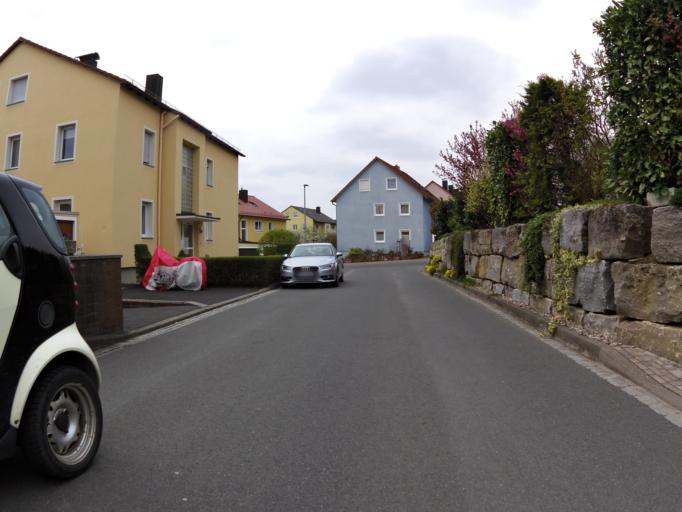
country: DE
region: Bavaria
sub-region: Regierungsbezirk Unterfranken
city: Rottendorf
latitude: 49.7988
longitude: 10.0260
